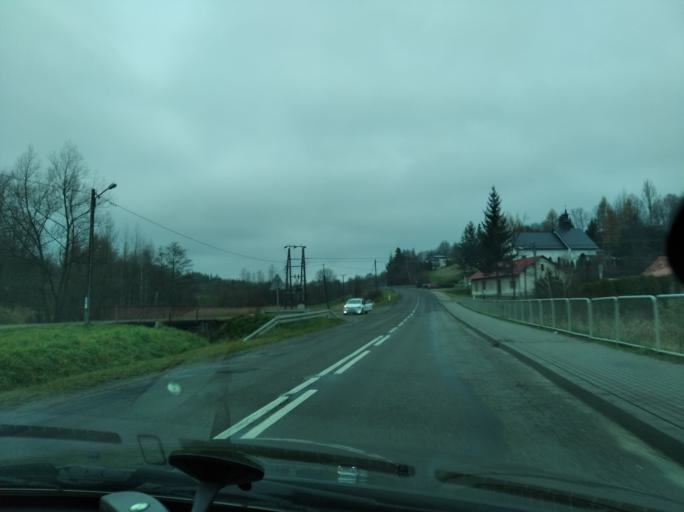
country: PL
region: Subcarpathian Voivodeship
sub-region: Powiat przeworski
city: Jawornik Polski
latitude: 49.8794
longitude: 22.2436
